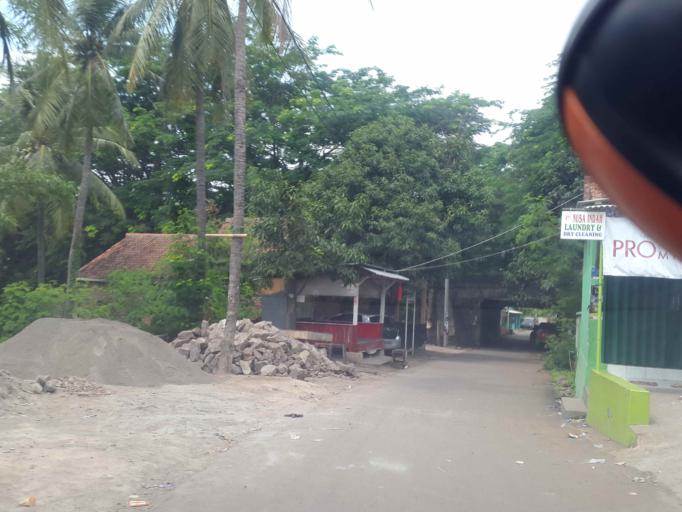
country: ID
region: Banten
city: Curug
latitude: -5.9789
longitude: 106.0136
